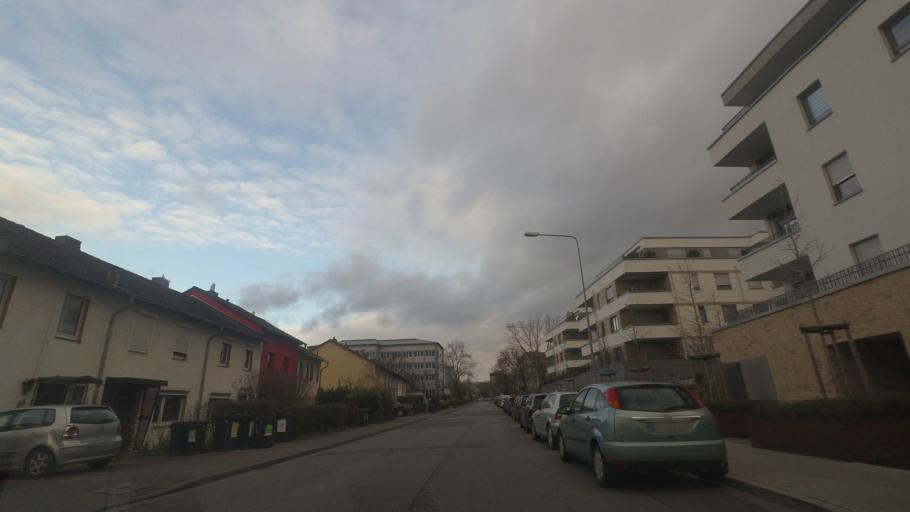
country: DE
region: Hesse
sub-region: Regierungsbezirk Darmstadt
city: Wiesbaden
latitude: 50.0640
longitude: 8.2602
